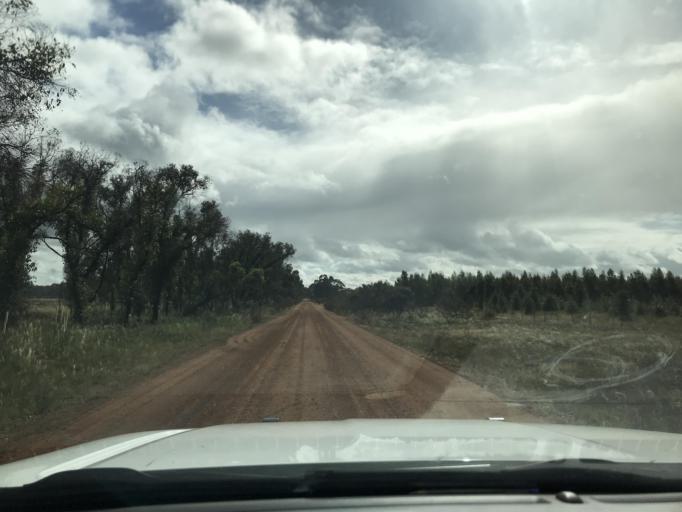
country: AU
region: South Australia
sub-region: Wattle Range
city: Penola
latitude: -37.1888
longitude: 141.1895
